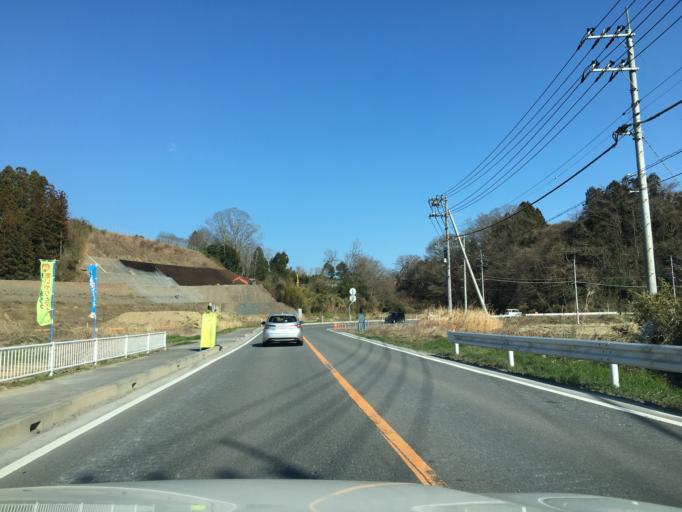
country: JP
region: Ibaraki
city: Omiya
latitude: 36.5549
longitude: 140.3204
